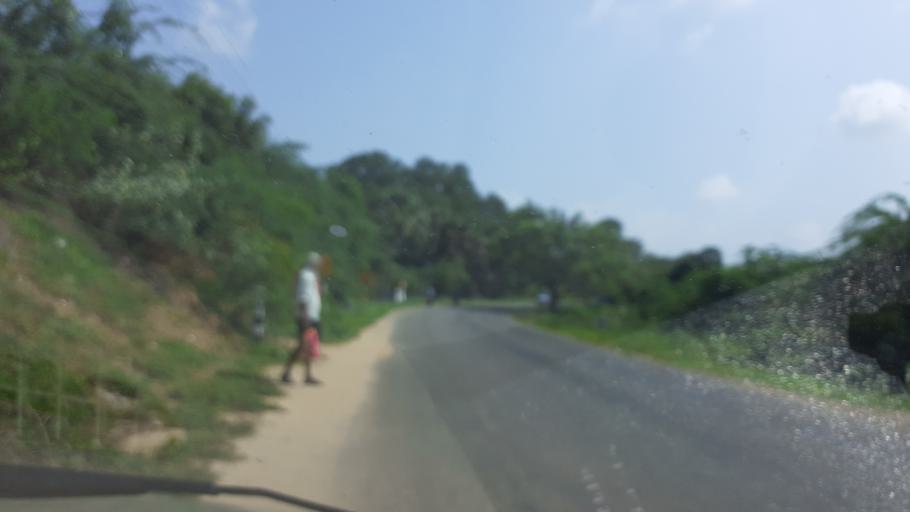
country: IN
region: Tamil Nadu
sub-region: Thoothukkudi
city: Srivaikuntam
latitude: 8.6322
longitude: 77.8795
